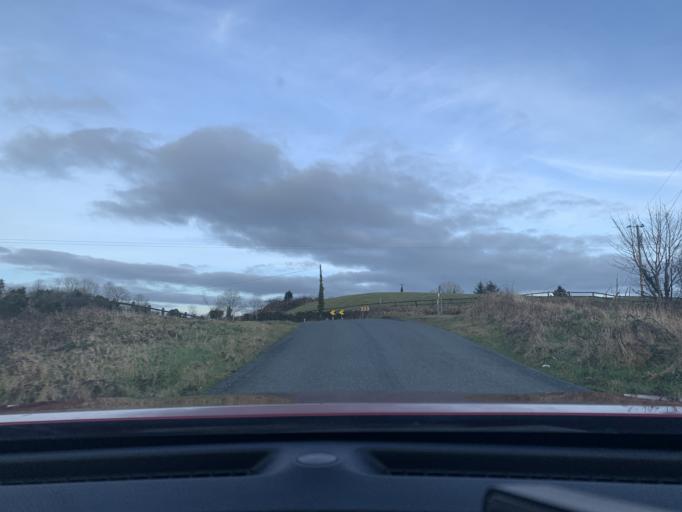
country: IE
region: Connaught
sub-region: Sligo
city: Ballymote
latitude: 54.1264
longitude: -8.5853
